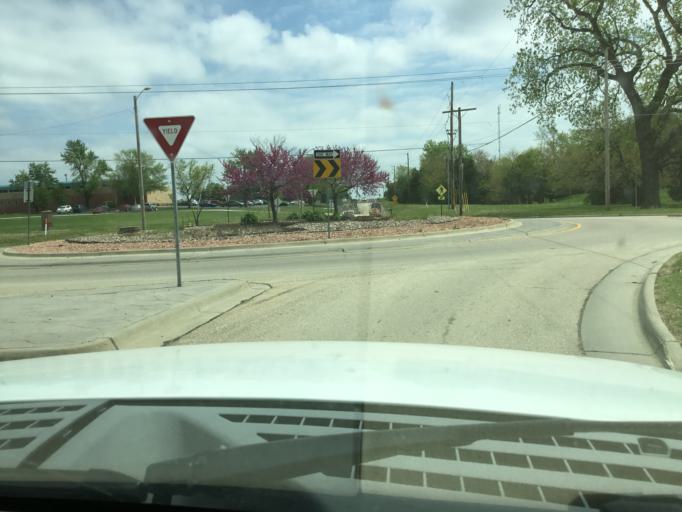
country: US
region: Kansas
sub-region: Shawnee County
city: Auburn
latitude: 38.9710
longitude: -95.7626
